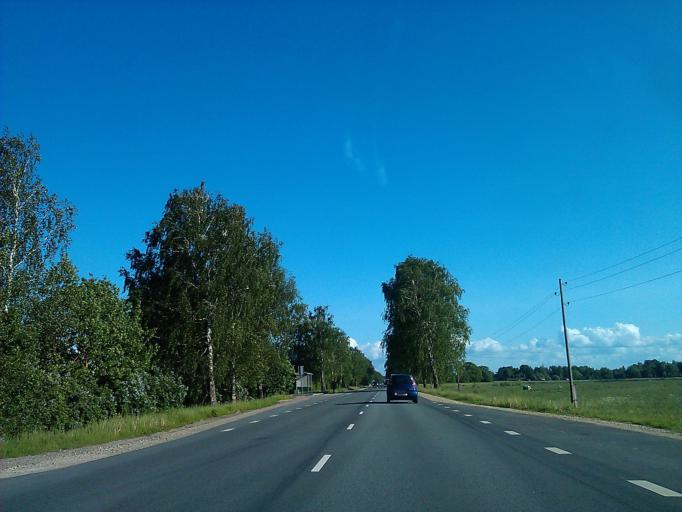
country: LV
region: Adazi
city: Adazi
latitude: 57.0887
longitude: 24.3152
